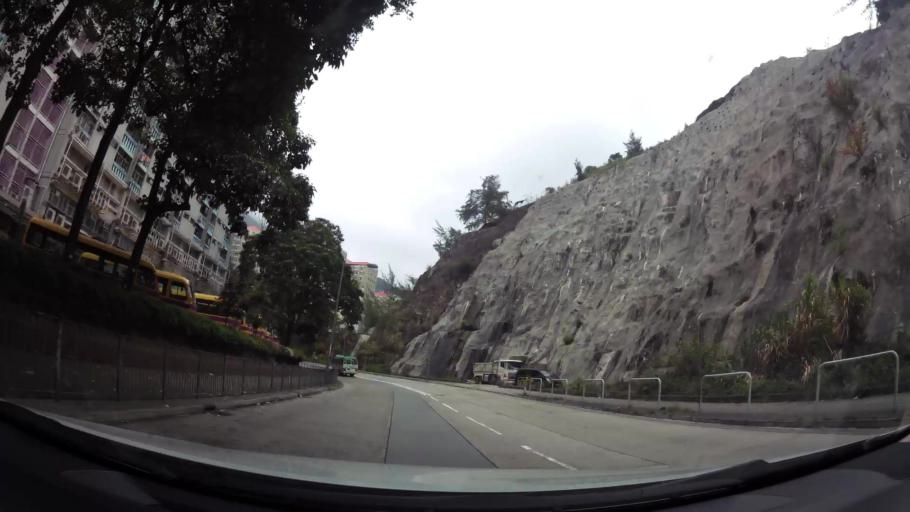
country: HK
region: Kowloon City
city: Kowloon
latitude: 22.3301
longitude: 114.2273
